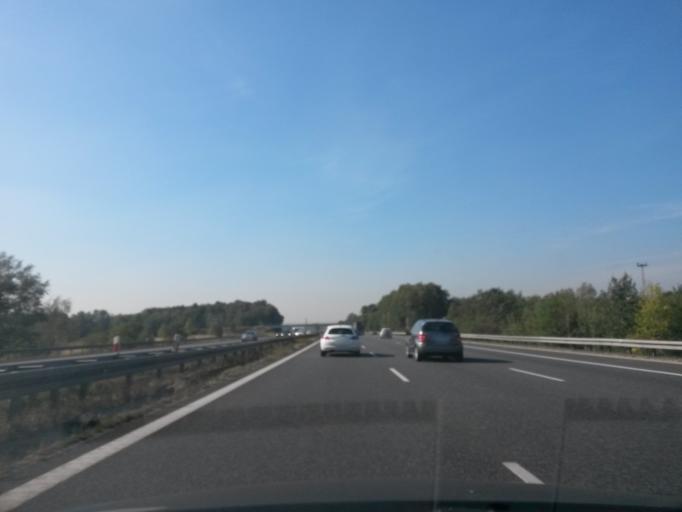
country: PL
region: Silesian Voivodeship
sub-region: Ruda Slaska
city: Ruda Slaska
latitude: 50.2584
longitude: 18.8363
